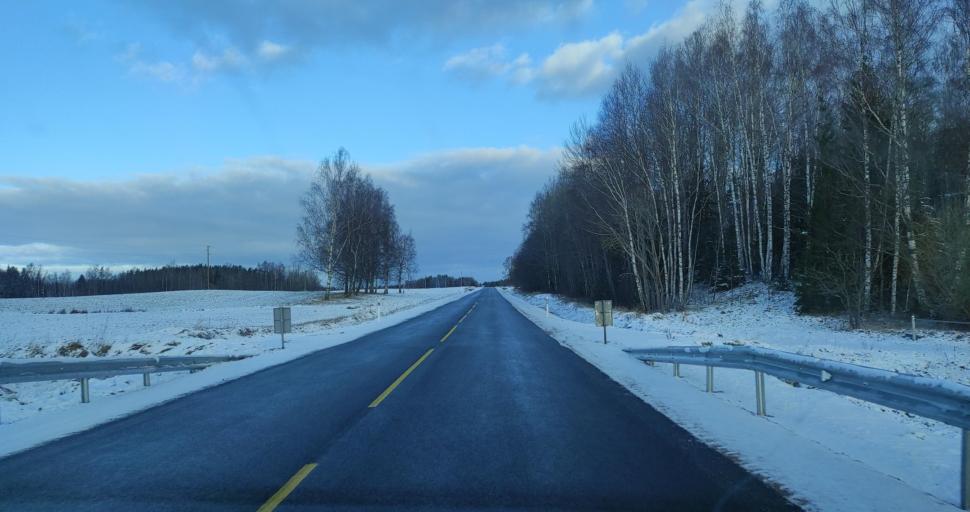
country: LV
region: Skrunda
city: Skrunda
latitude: 56.7155
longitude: 22.0107
